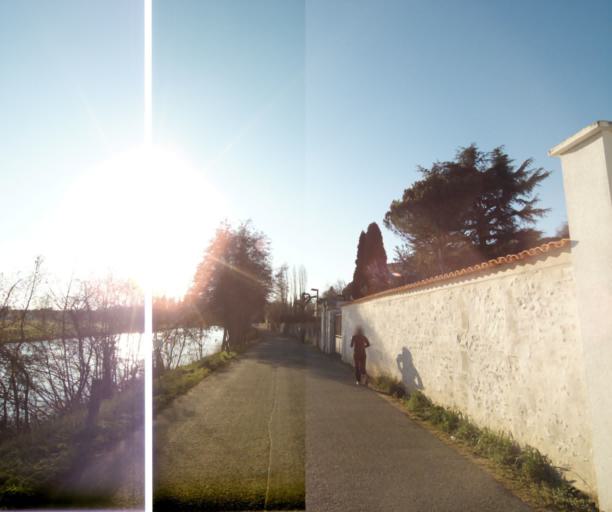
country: FR
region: Poitou-Charentes
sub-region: Departement des Deux-Sevres
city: Niort
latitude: 46.3363
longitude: -0.4865
